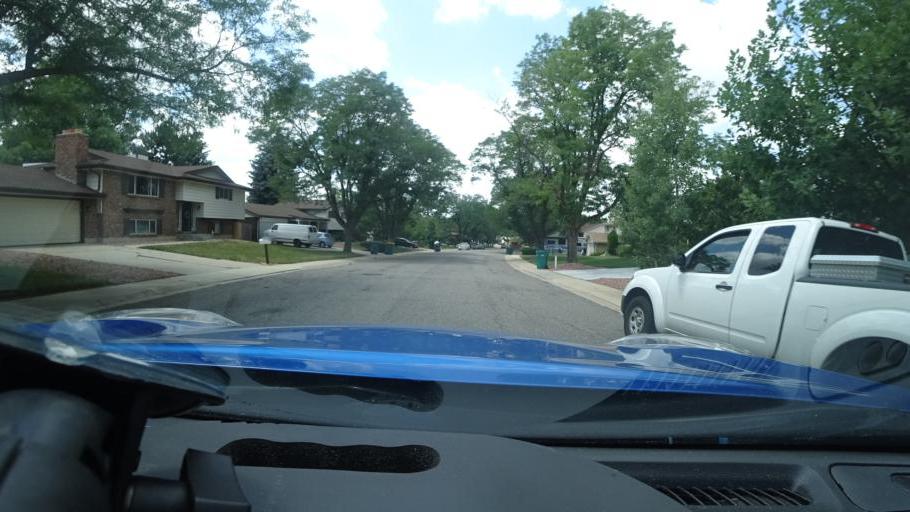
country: US
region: Colorado
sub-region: Adams County
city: Aurora
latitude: 39.7032
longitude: -104.8359
